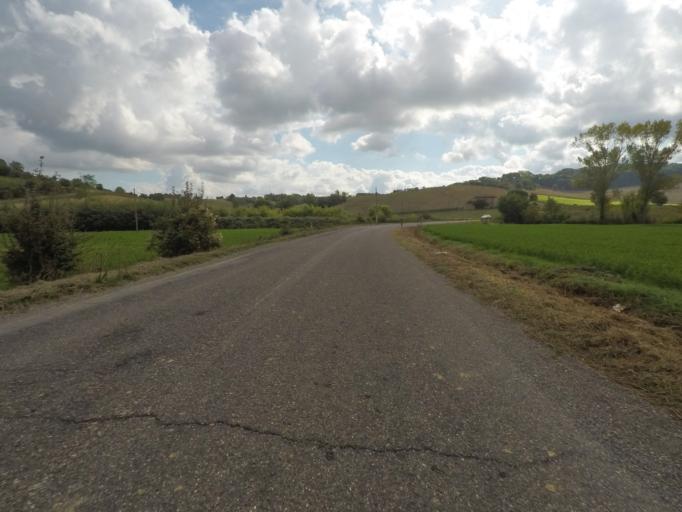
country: IT
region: Tuscany
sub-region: Provincia di Siena
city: Torrita di Siena
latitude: 43.1608
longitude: 11.7728
